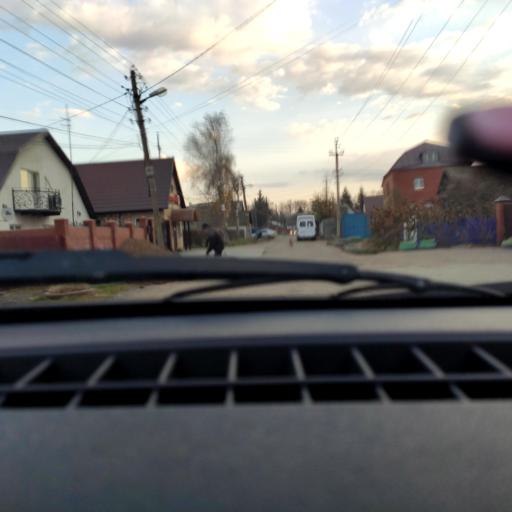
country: RU
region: Bashkortostan
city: Iglino
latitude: 54.8333
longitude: 56.1874
